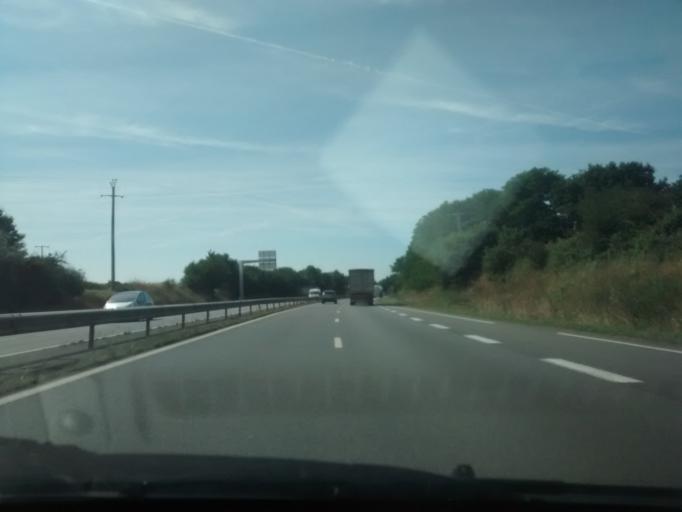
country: FR
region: Brittany
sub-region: Departement des Cotes-d'Armor
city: Plestan
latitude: 48.4194
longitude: -2.4450
